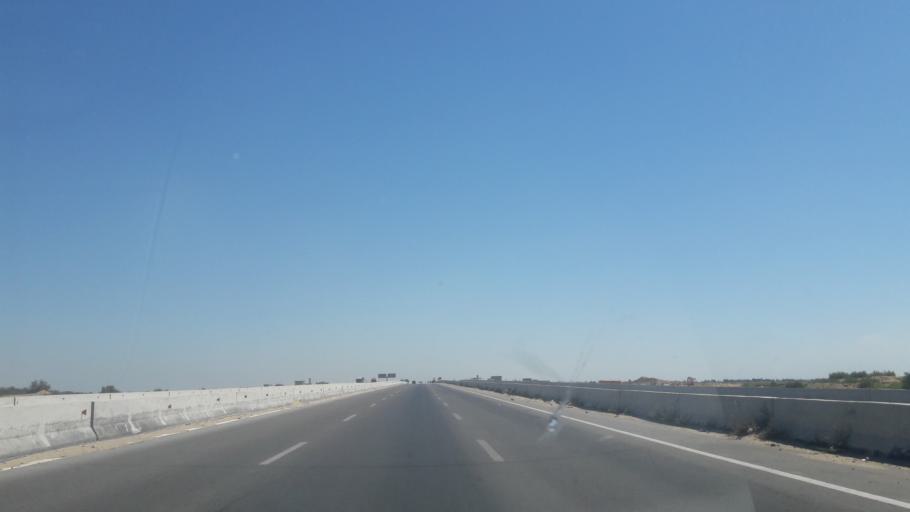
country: EG
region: Al Isma'iliyah
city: Ismailia
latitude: 30.8500
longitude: 32.1668
